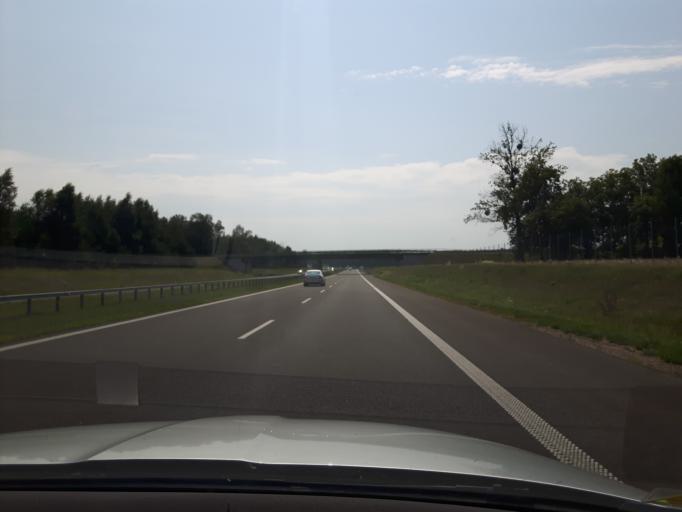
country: PL
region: Masovian Voivodeship
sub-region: Powiat mlawski
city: Wieczfnia Koscielna
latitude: 53.2648
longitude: 20.4295
